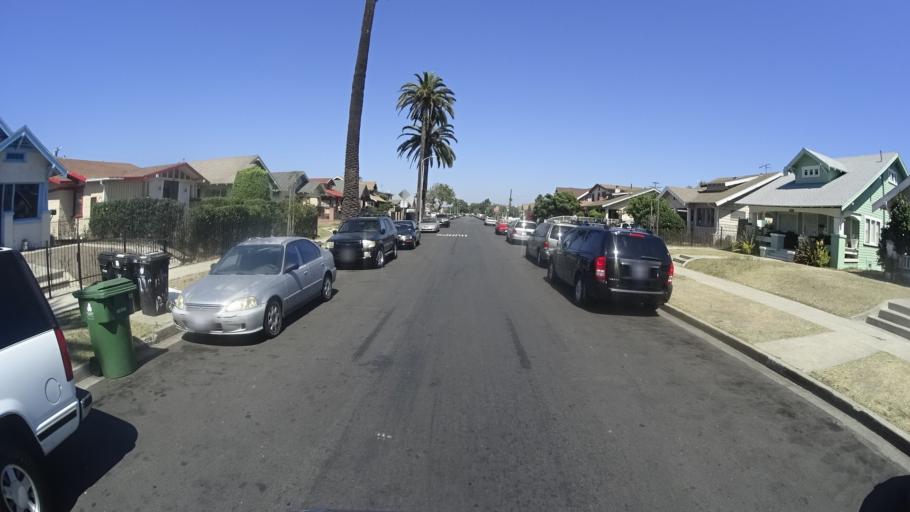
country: US
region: California
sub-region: Los Angeles County
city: View Park-Windsor Hills
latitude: 33.9941
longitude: -118.2970
